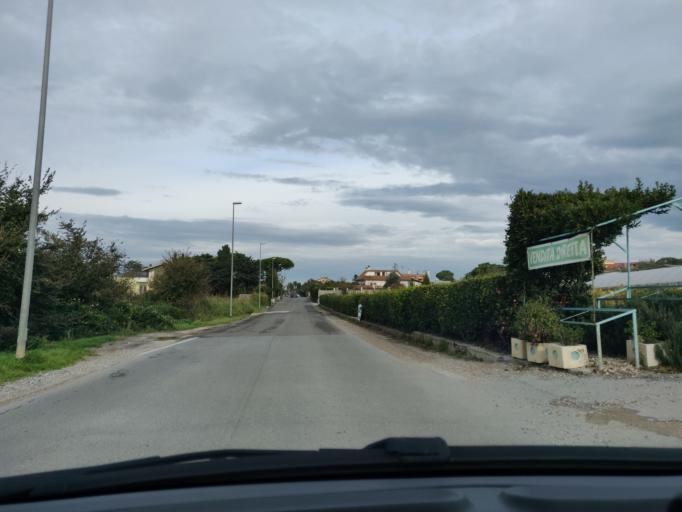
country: IT
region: Latium
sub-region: Citta metropolitana di Roma Capitale
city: Civitavecchia
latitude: 42.1020
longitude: 11.8128
